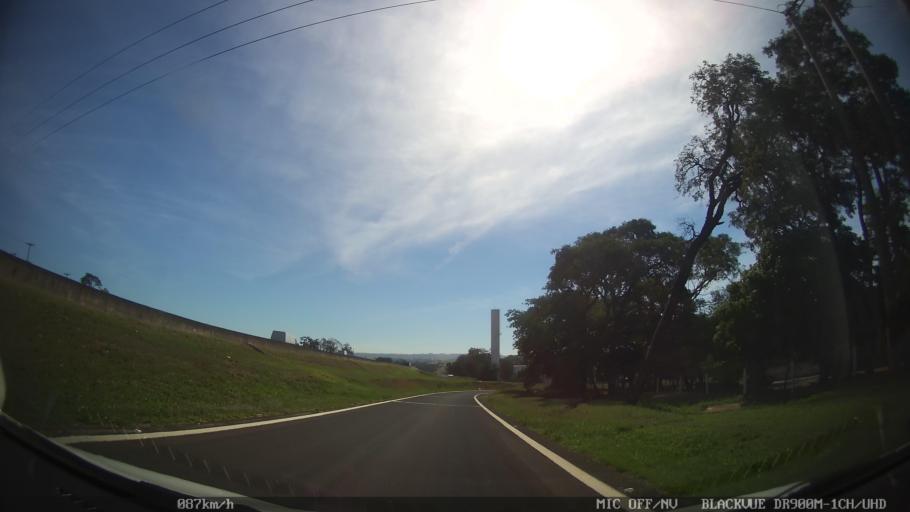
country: BR
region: Sao Paulo
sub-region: Porto Ferreira
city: Porto Ferreira
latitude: -21.8523
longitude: -47.4949
